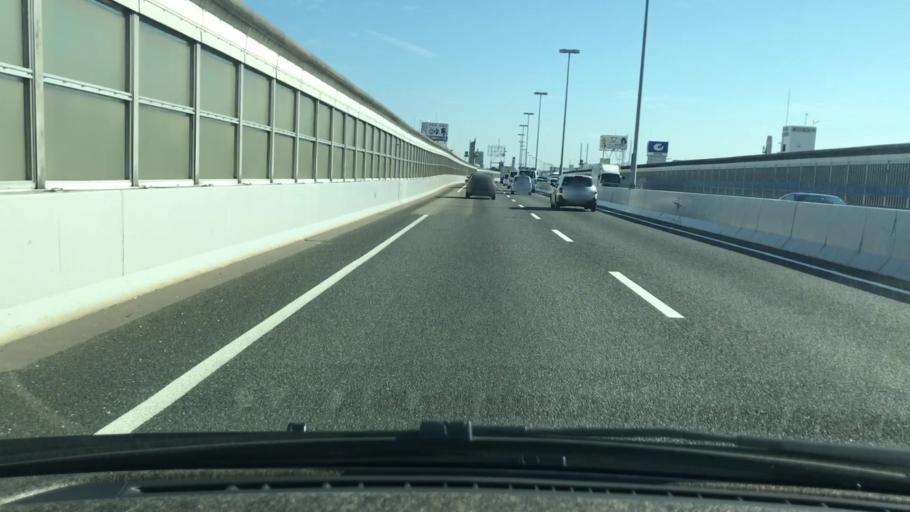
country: JP
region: Hyogo
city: Ashiya
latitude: 34.7112
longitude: 135.2556
